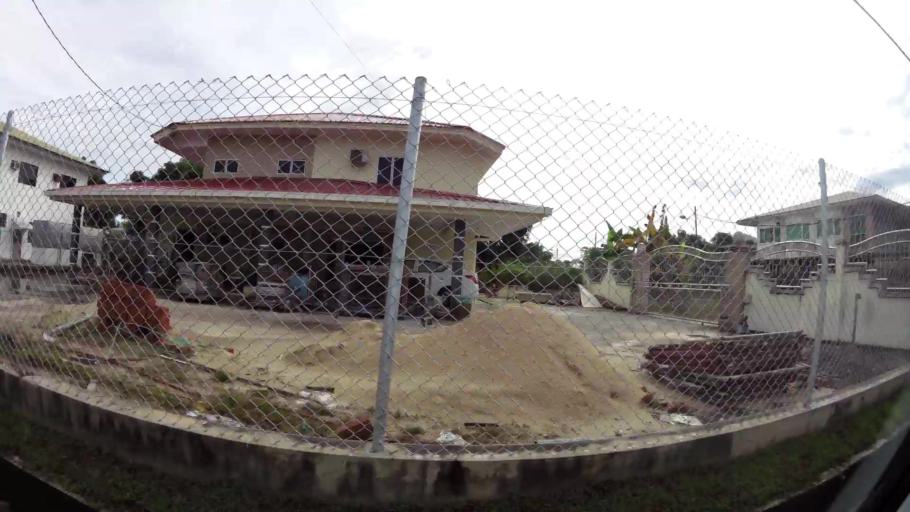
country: BN
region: Belait
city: Seria
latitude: 4.6135
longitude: 114.3609
